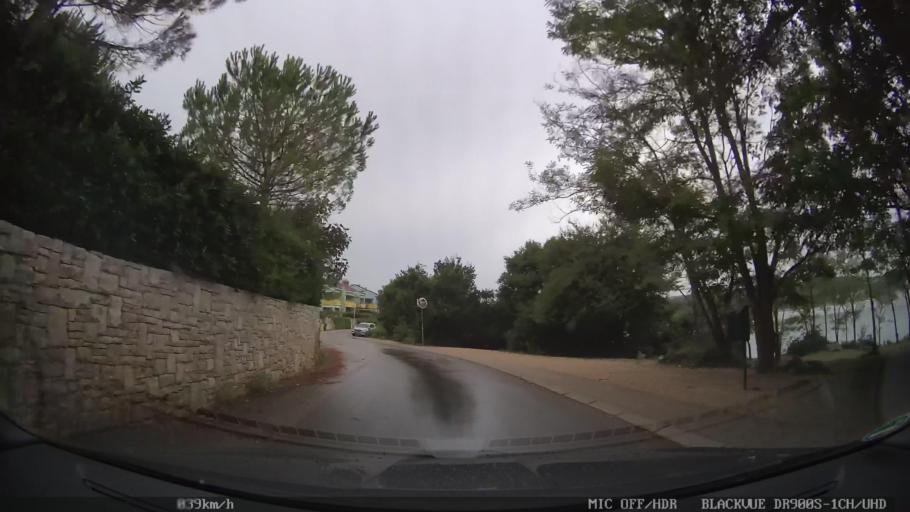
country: HR
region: Primorsko-Goranska
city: Njivice
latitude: 45.1503
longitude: 14.6066
